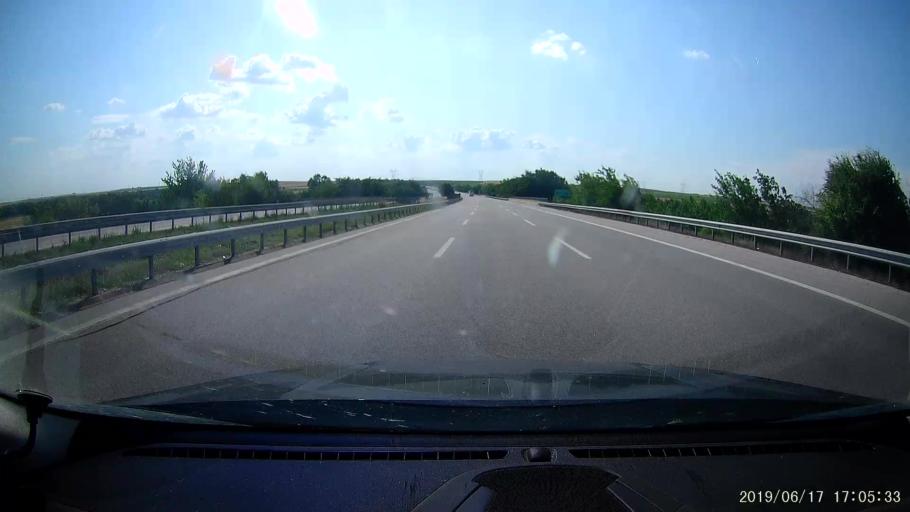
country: TR
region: Edirne
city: Edirne
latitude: 41.6606
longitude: 26.6961
